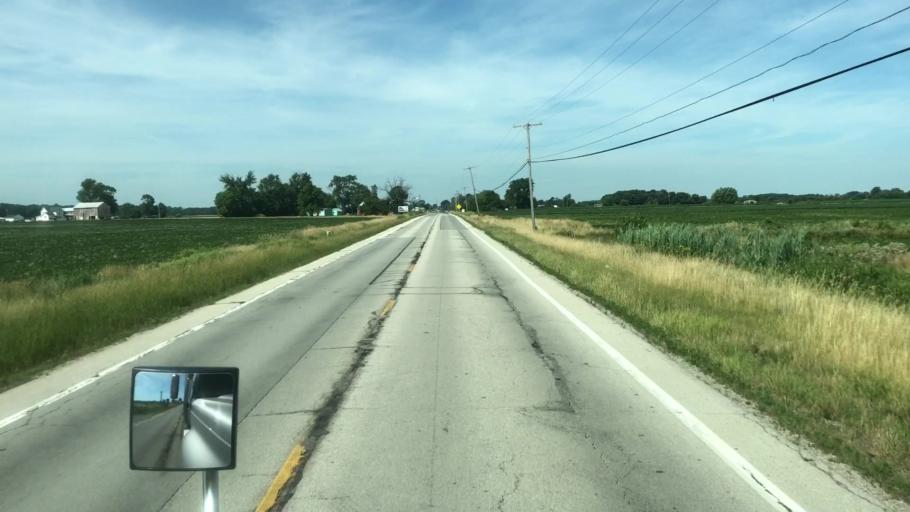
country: US
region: Ohio
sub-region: Ottawa County
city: Port Clinton
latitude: 41.4278
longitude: -82.8579
